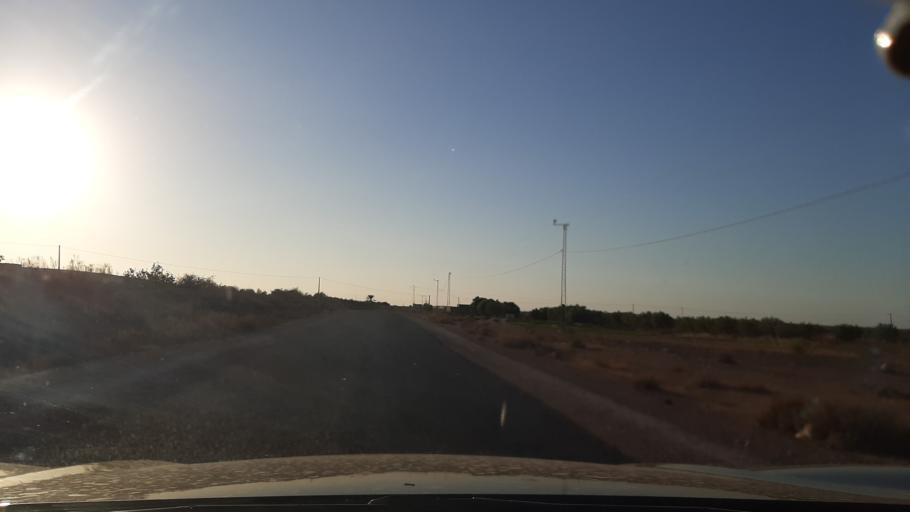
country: TN
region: Qabis
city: Matmata
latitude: 33.6183
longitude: 10.1470
